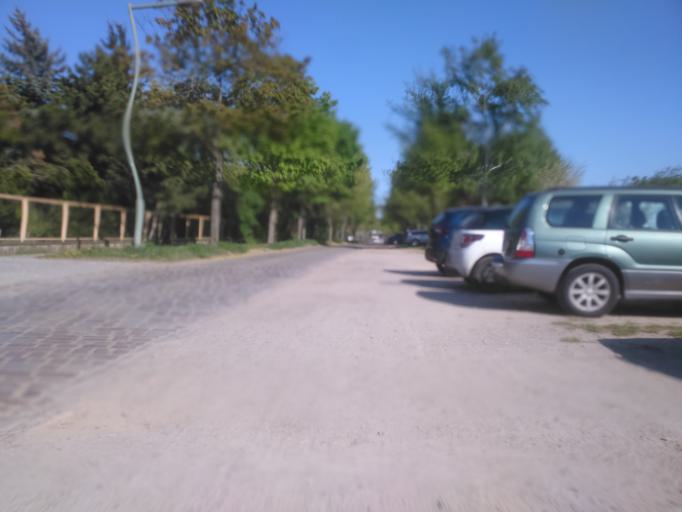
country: DE
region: Berlin
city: Alt-Hohenschoenhausen
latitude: 52.5619
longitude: 13.4893
